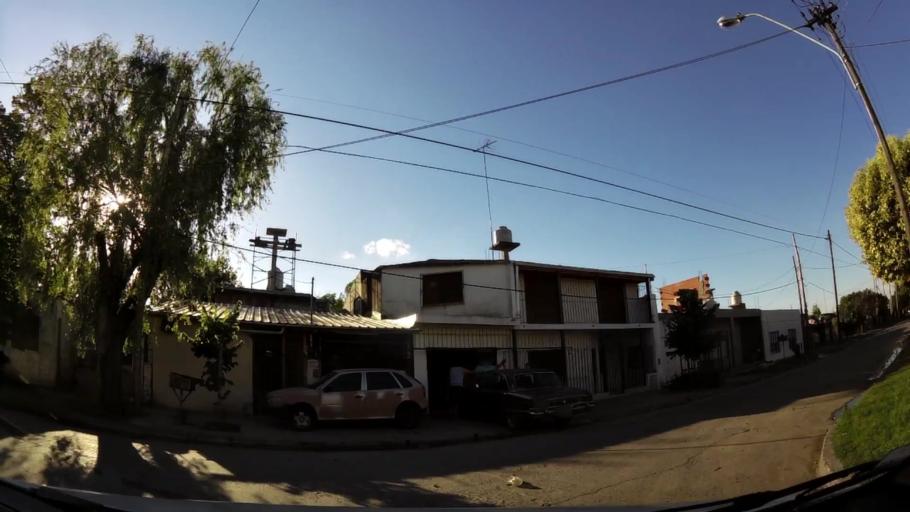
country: AR
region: Buenos Aires
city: Ituzaingo
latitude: -34.6922
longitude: -58.6433
